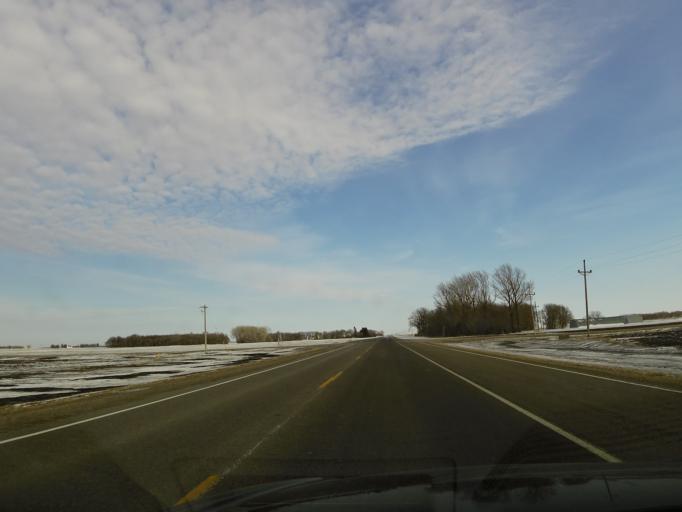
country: US
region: Minnesota
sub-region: Kittson County
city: Hallock
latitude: 48.5729
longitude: -97.1299
